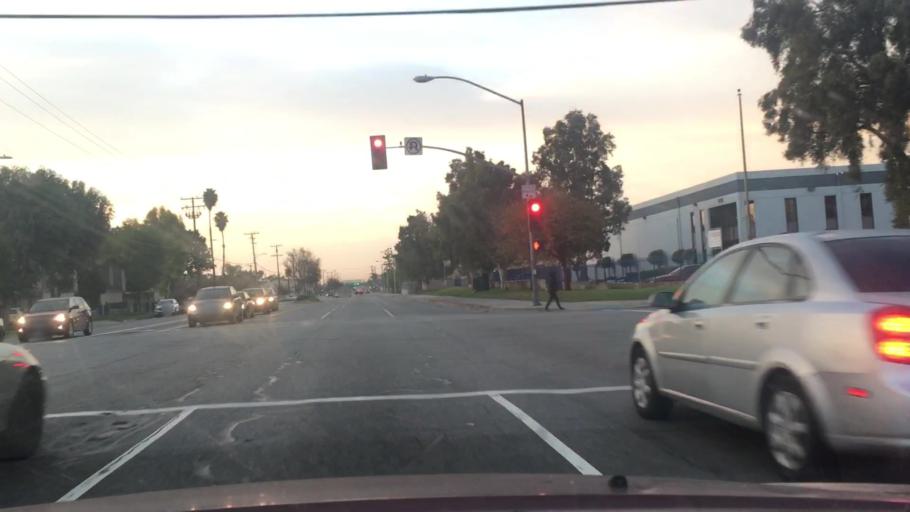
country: US
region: California
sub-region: Orange County
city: Buena Park
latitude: 33.8633
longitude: -118.0114
